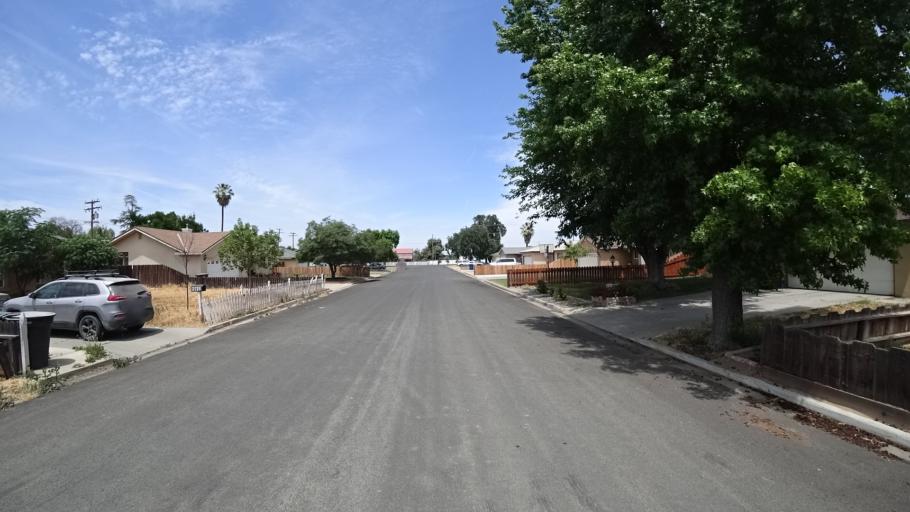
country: US
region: California
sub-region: Kings County
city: Armona
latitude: 36.3162
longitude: -119.7152
